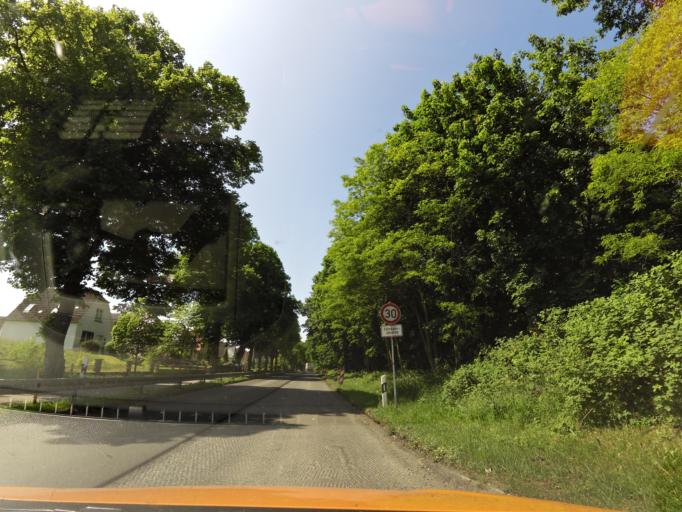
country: DE
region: Mecklenburg-Vorpommern
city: Selmsdorf
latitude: 53.8839
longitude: 10.8466
